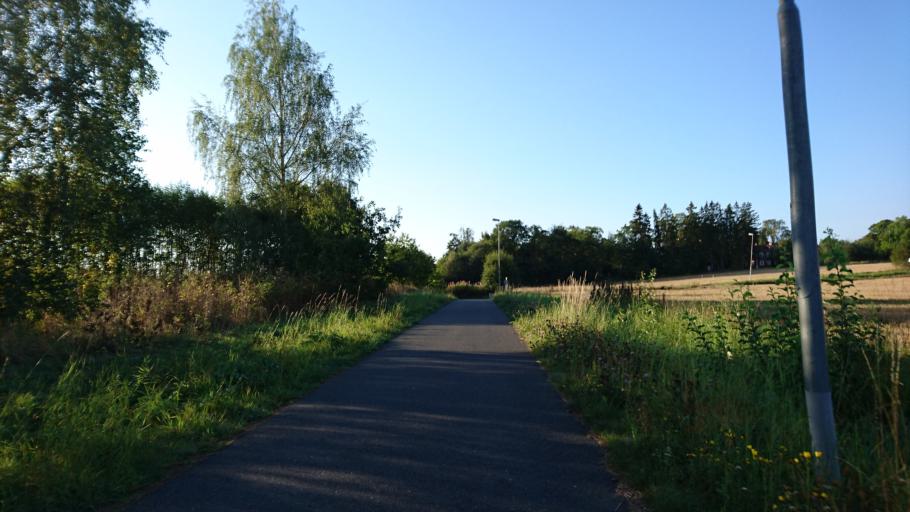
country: SE
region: Joenkoeping
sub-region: Jonkopings Kommun
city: Bankeryd
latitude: 57.8225
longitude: 14.1478
